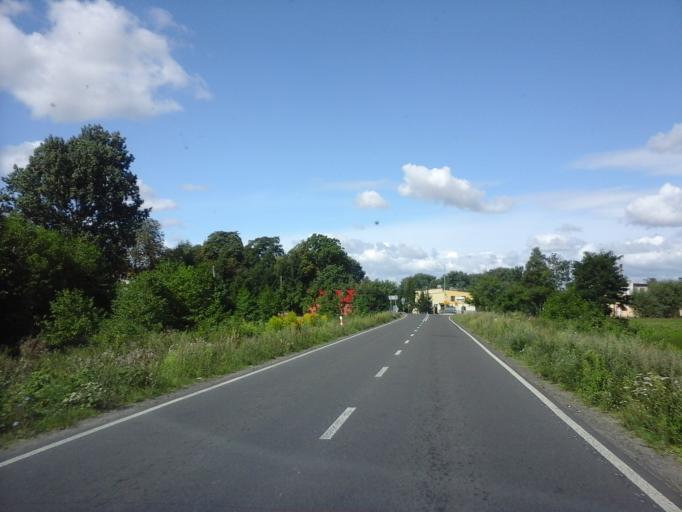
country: PL
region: West Pomeranian Voivodeship
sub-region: Powiat stargardzki
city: Dolice
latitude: 53.2316
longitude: 15.1191
